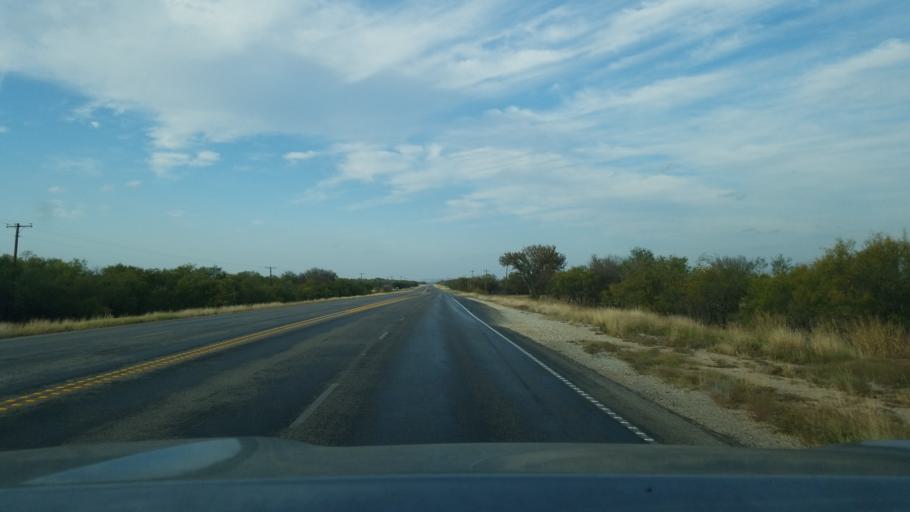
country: US
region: Texas
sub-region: Brown County
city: Early
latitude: 31.7827
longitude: -98.9473
